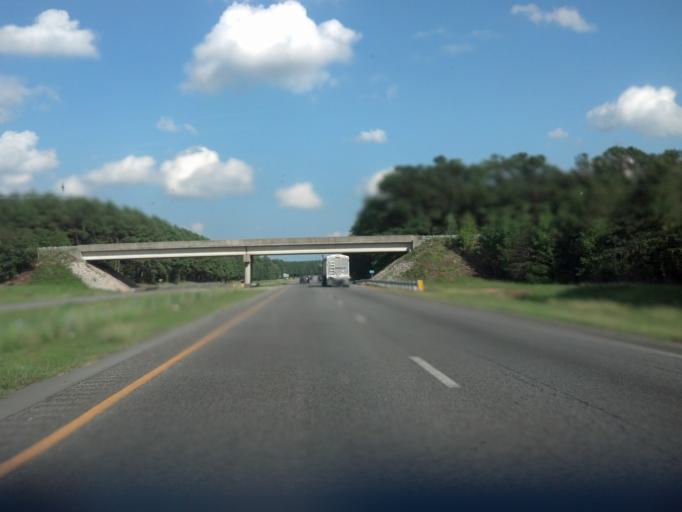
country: US
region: North Carolina
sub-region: Nash County
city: Rocky Mount
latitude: 35.9355
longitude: -77.7318
